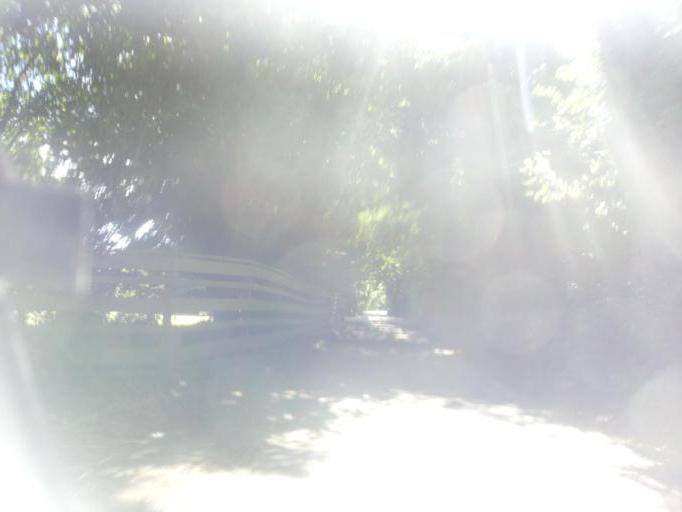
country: GB
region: England
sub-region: Kent
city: Lenham
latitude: 51.2876
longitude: 0.7016
